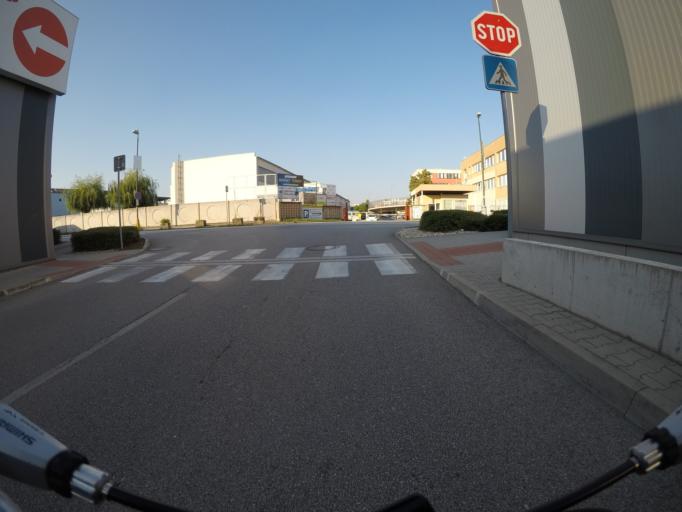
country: SK
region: Bratislavsky
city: Bratislava
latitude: 48.1705
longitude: 17.1827
